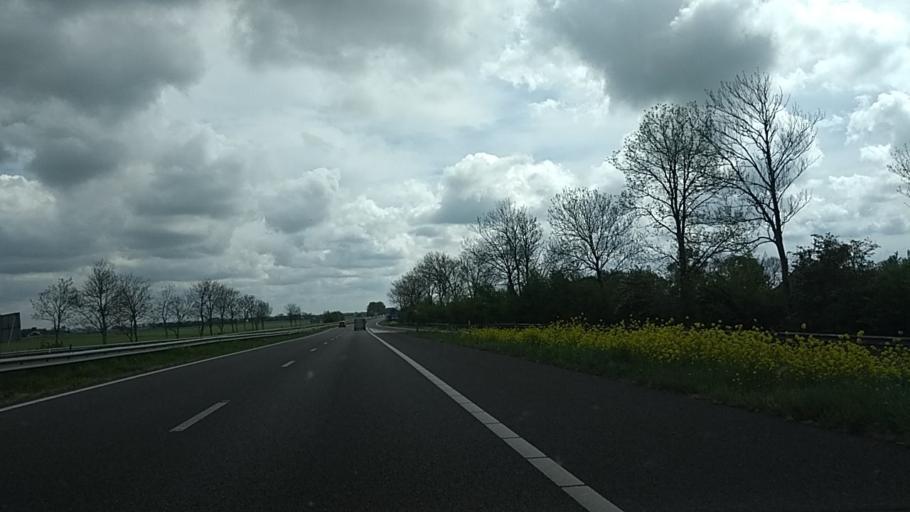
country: NL
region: Friesland
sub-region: Sudwest Fryslan
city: Bolsward
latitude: 53.0552
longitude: 5.5388
